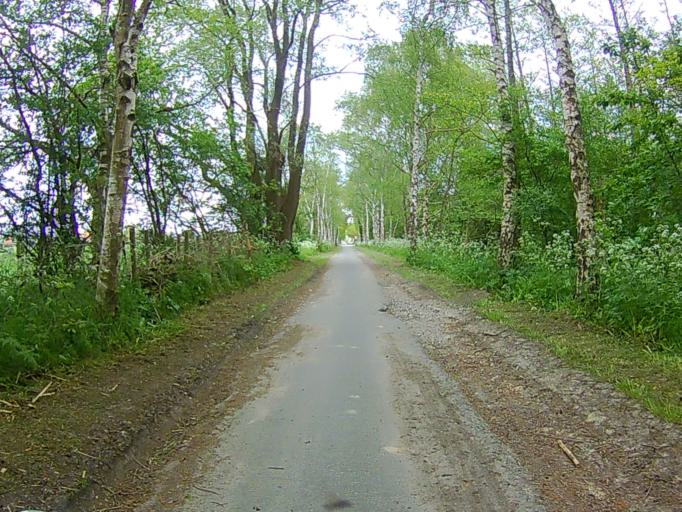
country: BE
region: Flanders
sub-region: Provincie Vlaams-Brabant
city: Merchtem
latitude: 50.9795
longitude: 4.2182
